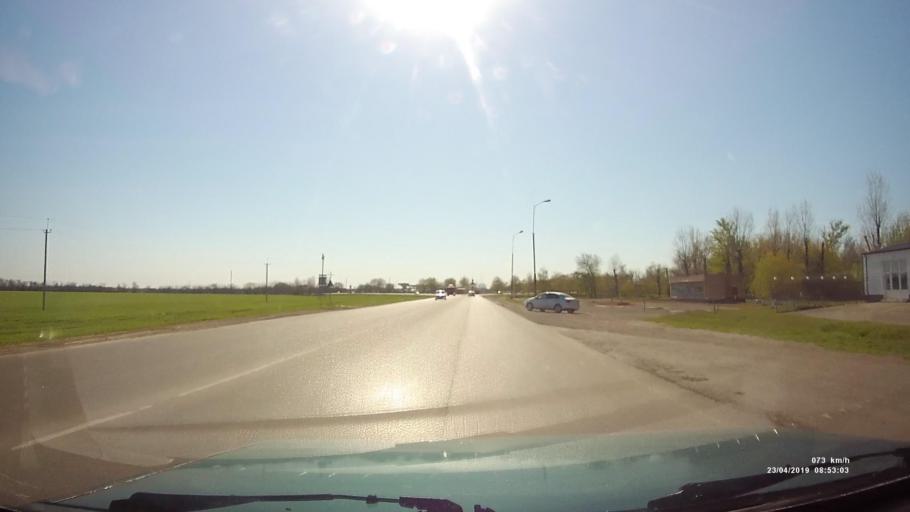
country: RU
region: Rostov
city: Sal'sk
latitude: 46.4777
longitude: 41.4696
